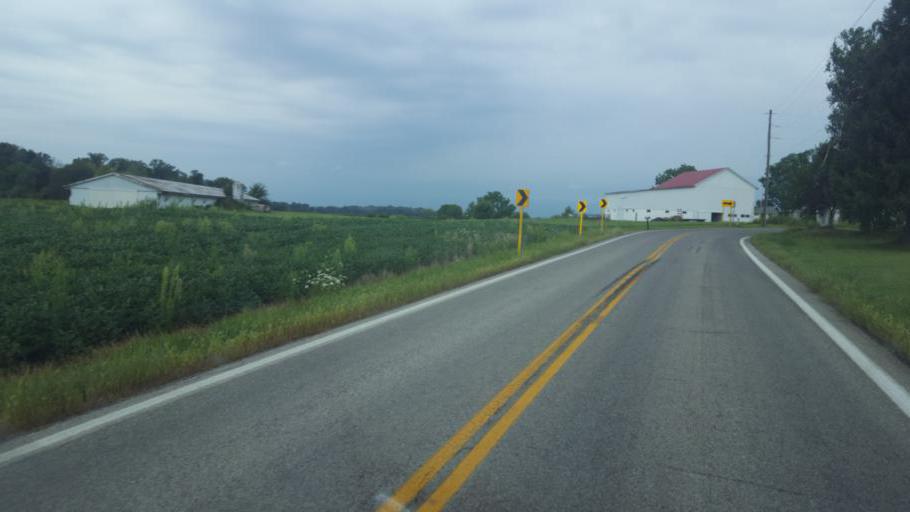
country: US
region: Ohio
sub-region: Morrow County
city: Mount Gilead
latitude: 40.5919
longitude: -82.7658
